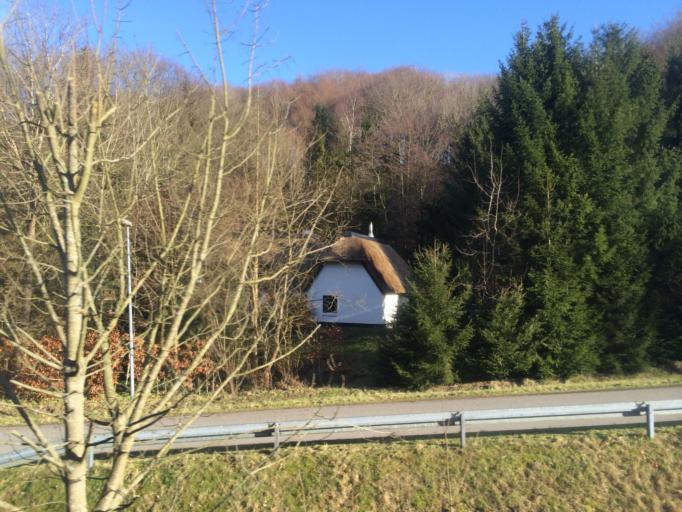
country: DK
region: South Denmark
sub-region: Vejle Kommune
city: Vejle
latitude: 55.7566
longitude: 9.5321
